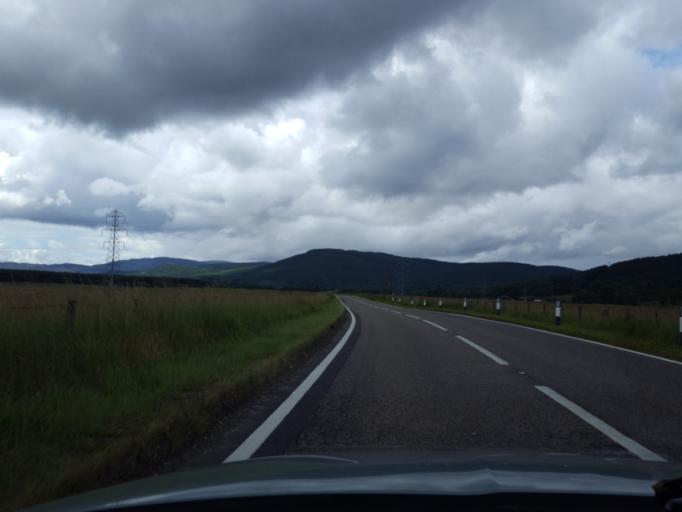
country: GB
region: Scotland
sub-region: Highland
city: Aviemore
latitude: 57.2574
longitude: -3.7587
